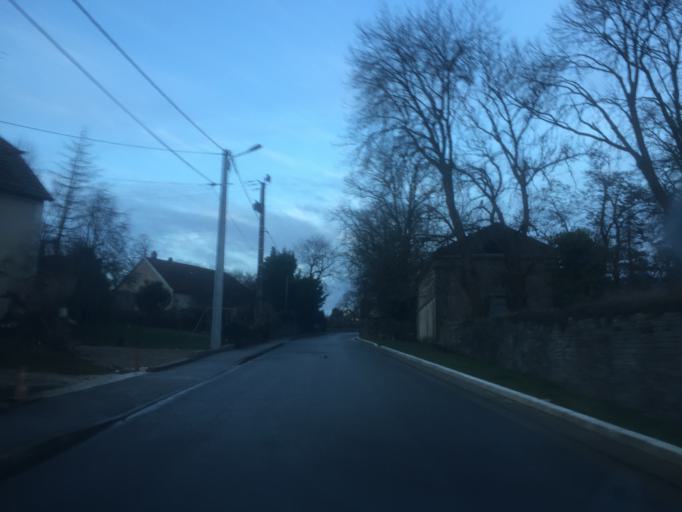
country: FR
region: Franche-Comte
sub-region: Departement du Jura
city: Orchamps
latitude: 47.1439
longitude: 5.6811
